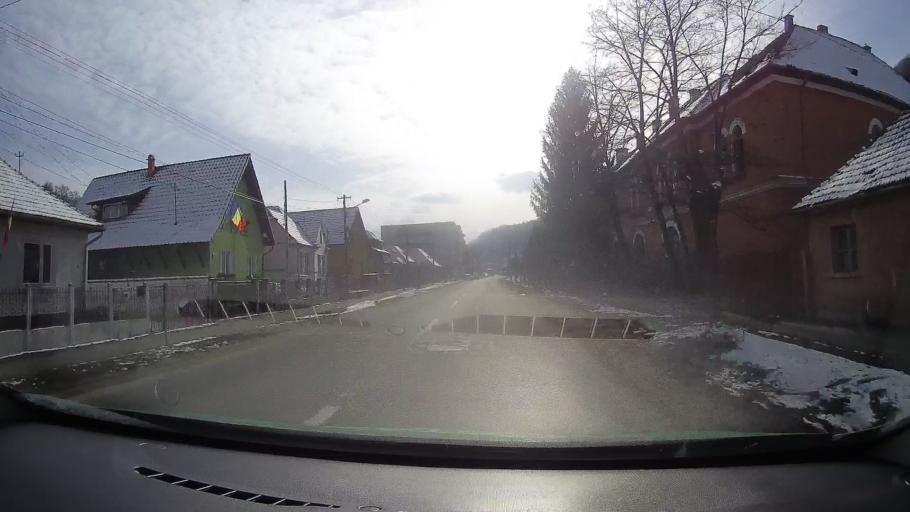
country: RO
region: Mures
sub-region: Municipiul Sighisoara
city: Sighisoara
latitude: 46.2132
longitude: 24.7819
